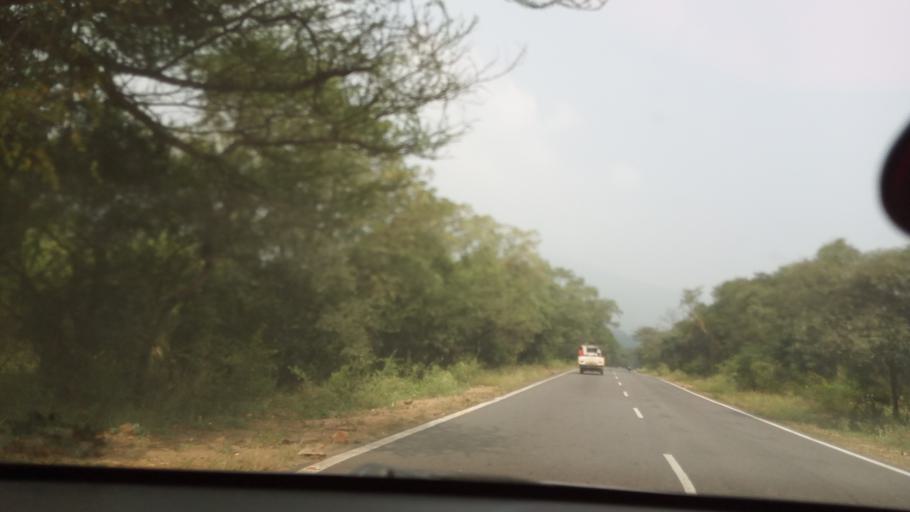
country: IN
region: Tamil Nadu
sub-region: Erode
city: Sathyamangalam
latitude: 11.5756
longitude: 77.1334
